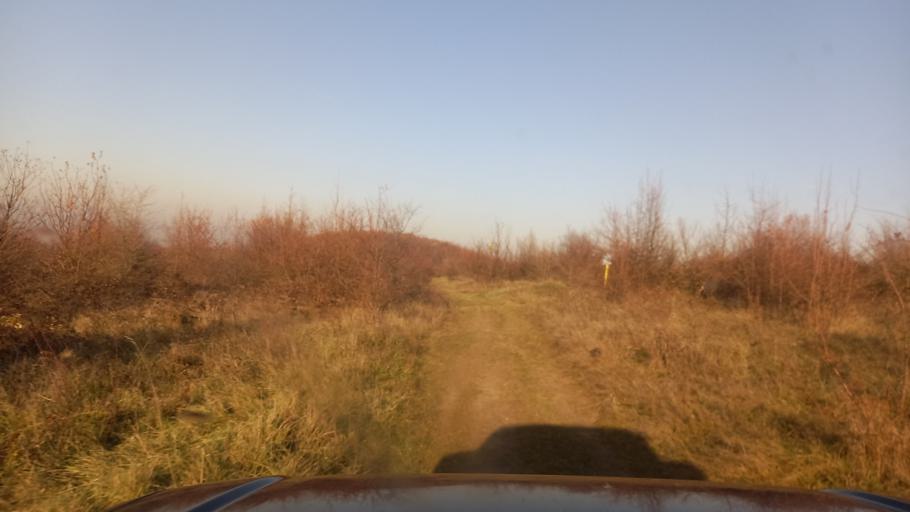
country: RU
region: Krasnodarskiy
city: Azovskaya
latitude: 44.8103
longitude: 38.5951
